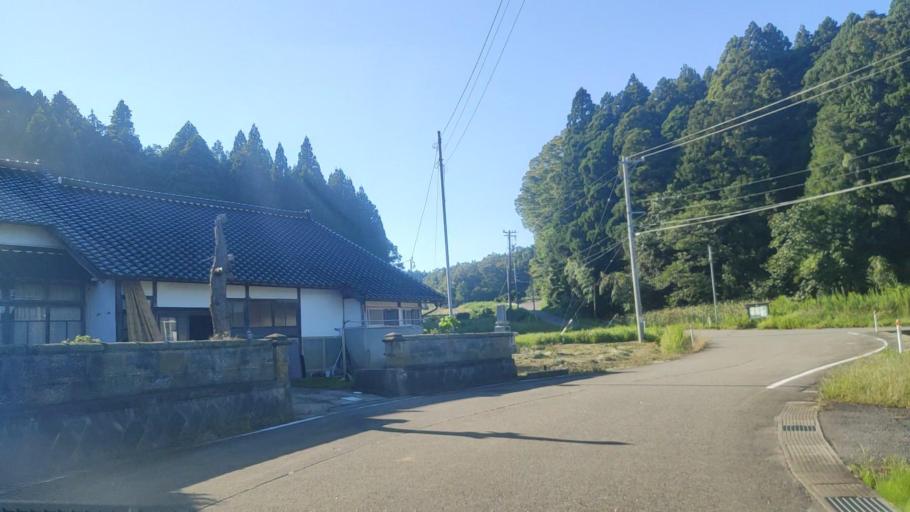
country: JP
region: Ishikawa
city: Nanao
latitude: 37.1281
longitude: 136.8957
